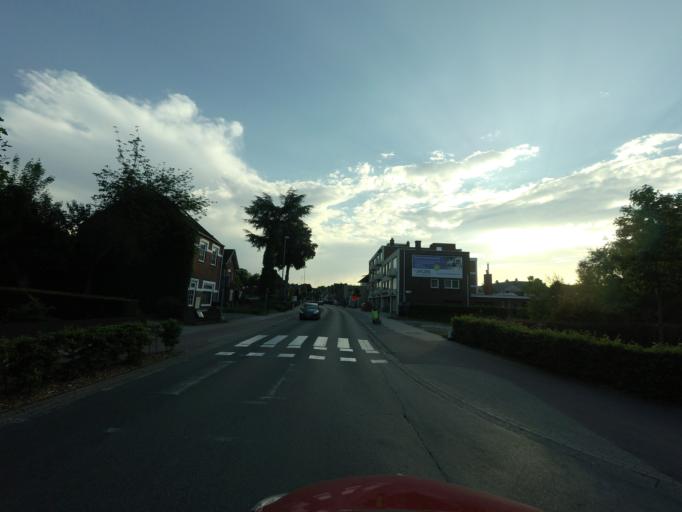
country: BE
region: Flanders
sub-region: Provincie Limburg
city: Lommel
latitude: 51.2287
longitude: 5.3186
